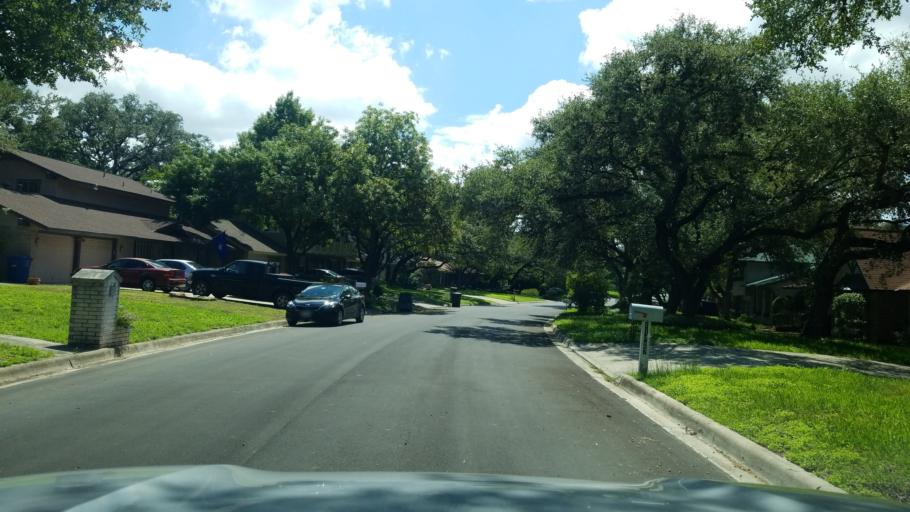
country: US
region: Texas
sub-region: Bexar County
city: Castle Hills
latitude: 29.5474
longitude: -98.4987
